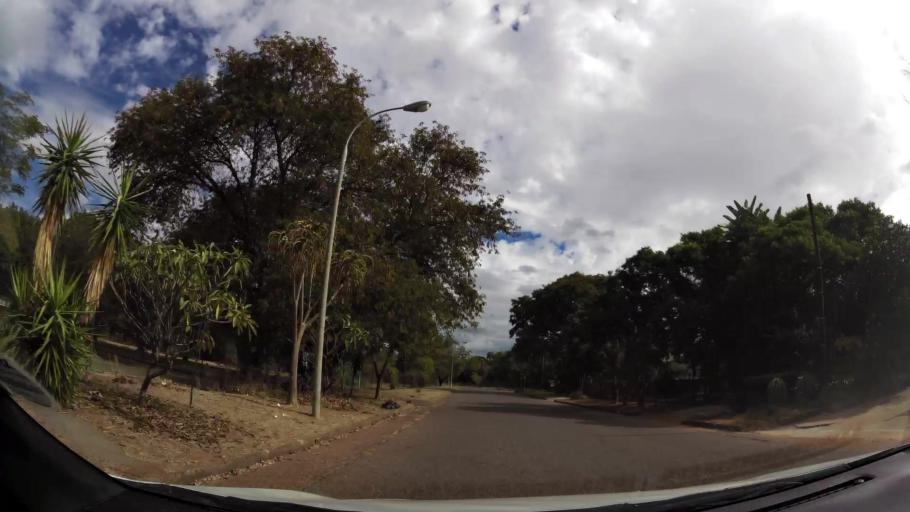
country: ZA
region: Limpopo
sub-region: Waterberg District Municipality
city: Warmbaths
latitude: -24.8879
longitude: 28.2813
